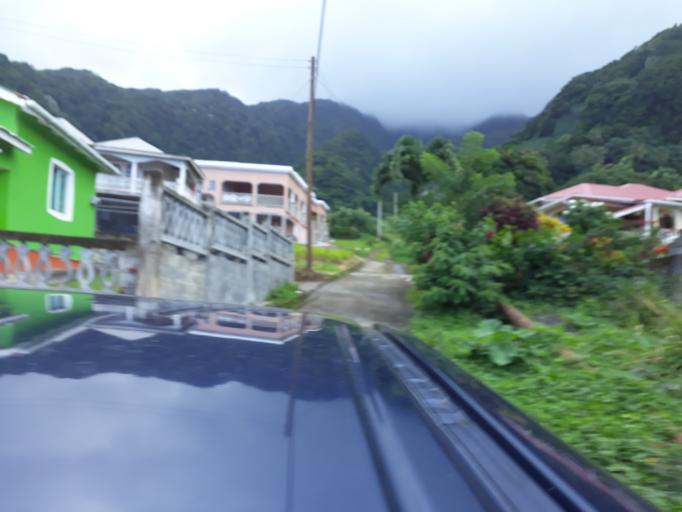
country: VC
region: Charlotte
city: Georgetown
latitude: 13.3776
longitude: -61.1700
